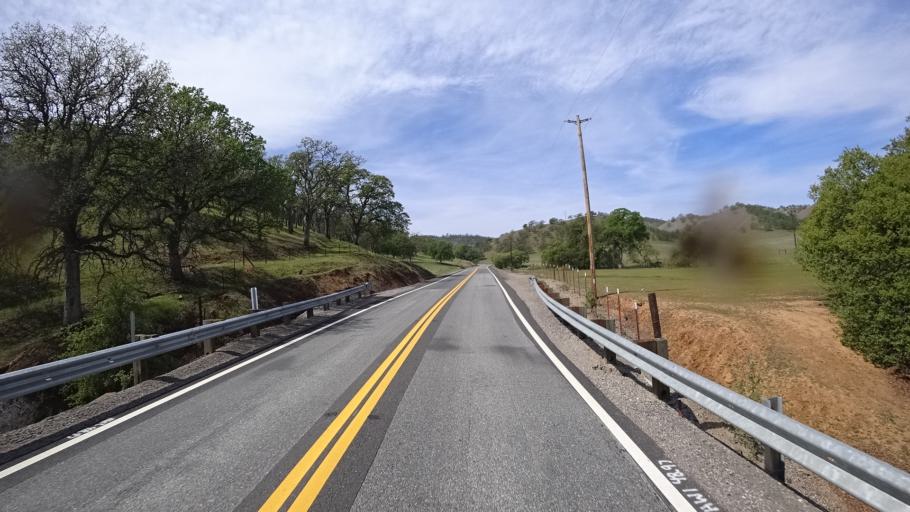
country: US
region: California
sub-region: Glenn County
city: Willows
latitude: 39.5981
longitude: -122.4790
